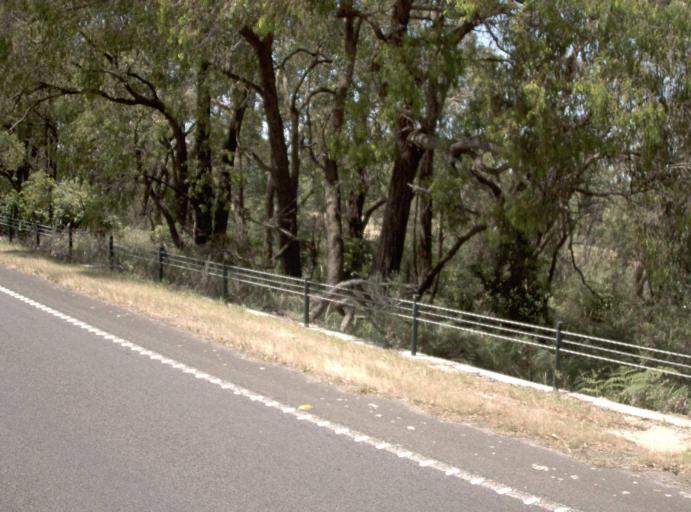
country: AU
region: Victoria
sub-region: Cardinia
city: Garfield
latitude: -38.0722
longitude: 145.6621
